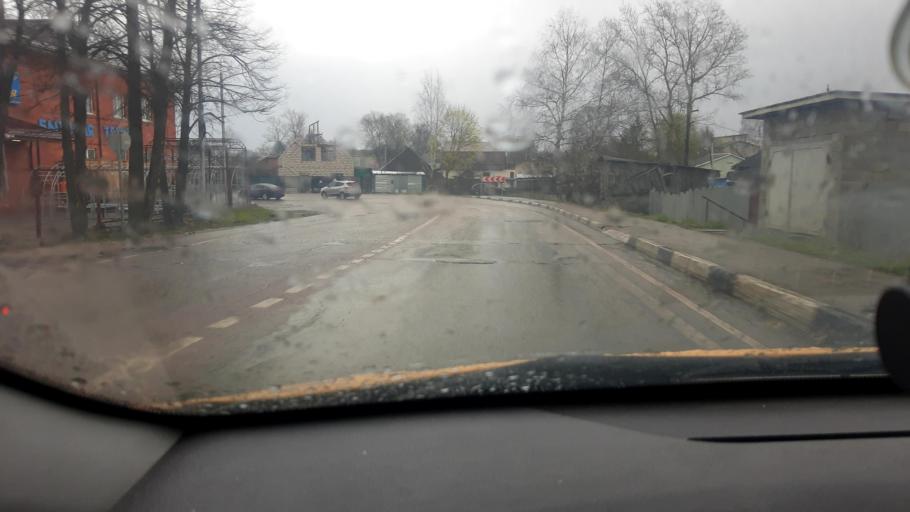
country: RU
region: Moskovskaya
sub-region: Volokolamskiy Rayon
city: Volokolamsk
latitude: 55.9953
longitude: 35.9297
